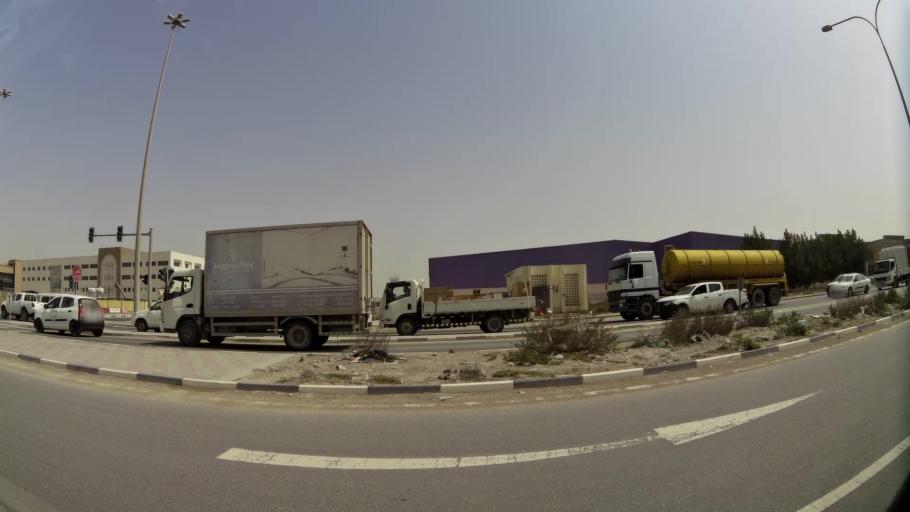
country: QA
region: Baladiyat ar Rayyan
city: Ar Rayyan
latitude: 25.1648
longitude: 51.4043
